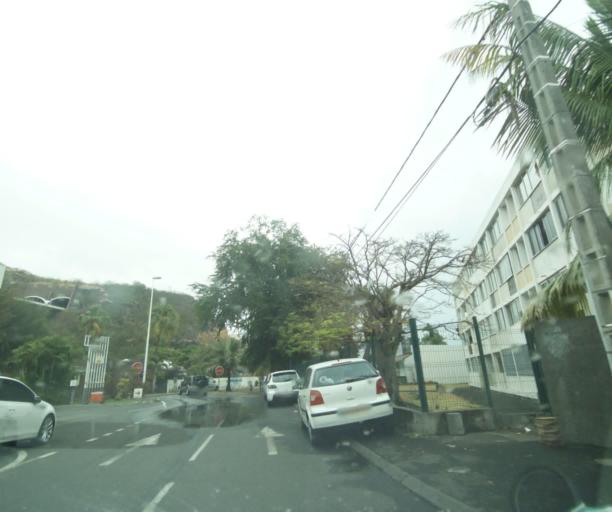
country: RE
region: Reunion
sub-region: Reunion
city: Saint-Paul
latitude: -21.0140
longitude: 55.2655
